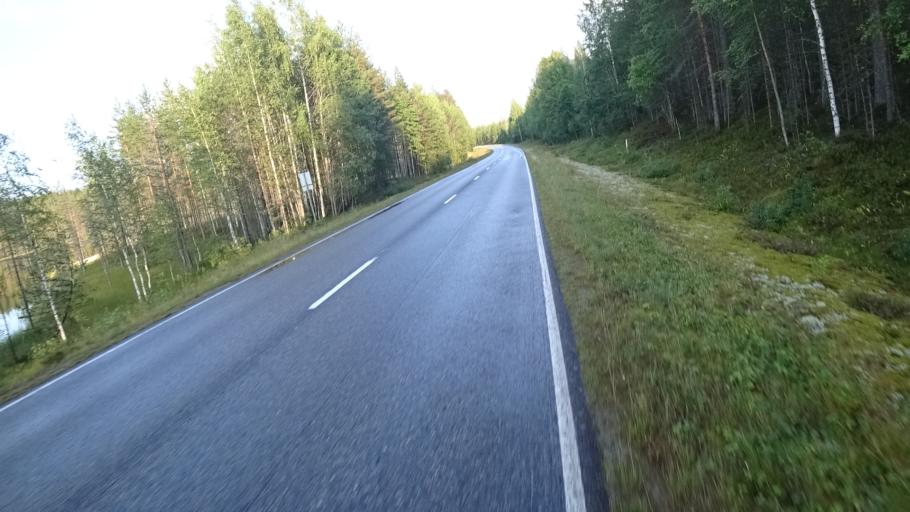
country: FI
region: North Karelia
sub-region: Joensuu
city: Ilomantsi
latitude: 62.6246
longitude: 31.1136
